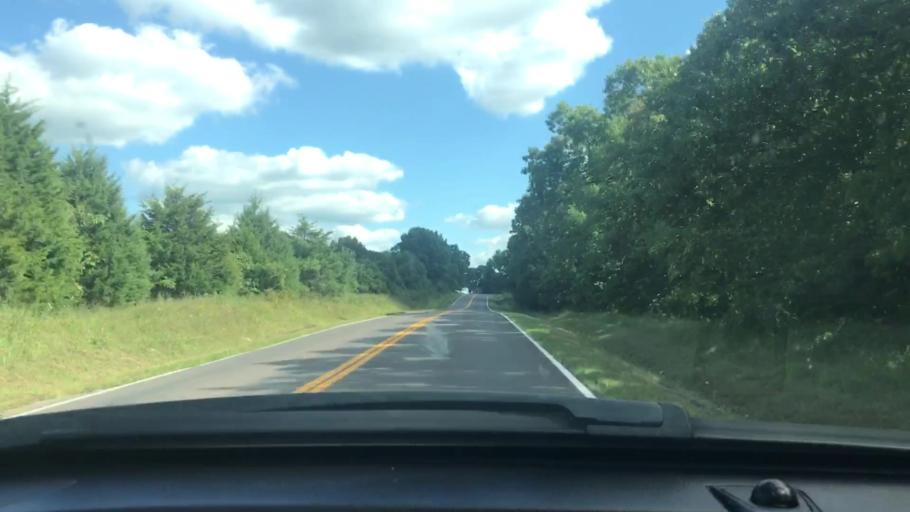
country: US
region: Missouri
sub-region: Wright County
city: Hartville
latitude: 37.3632
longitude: -92.3460
